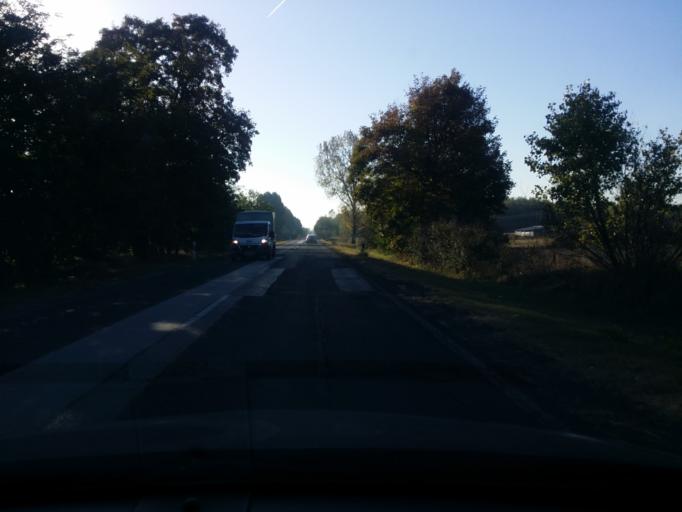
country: HU
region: Bacs-Kiskun
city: Nyarlorinc
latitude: 46.8787
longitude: 19.8459
